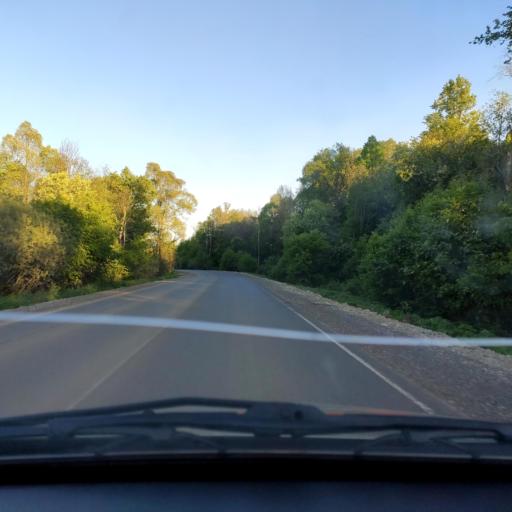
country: RU
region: Bashkortostan
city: Yazykovo
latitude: 55.0269
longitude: 56.2084
